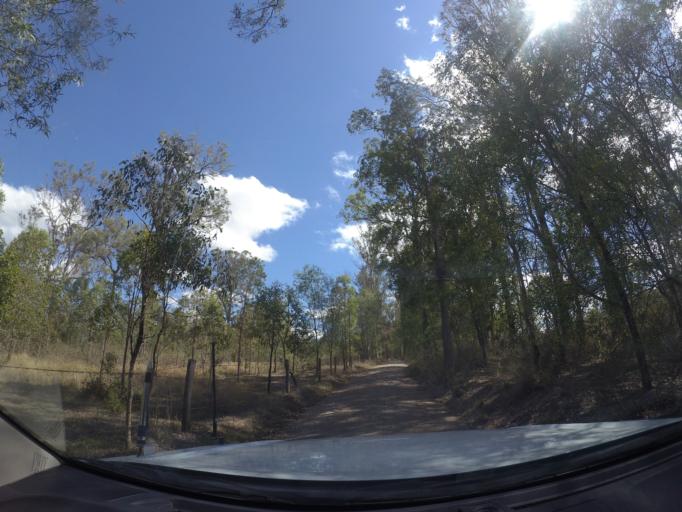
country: AU
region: Queensland
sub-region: Logan
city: Cedar Vale
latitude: -27.8431
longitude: 152.9738
